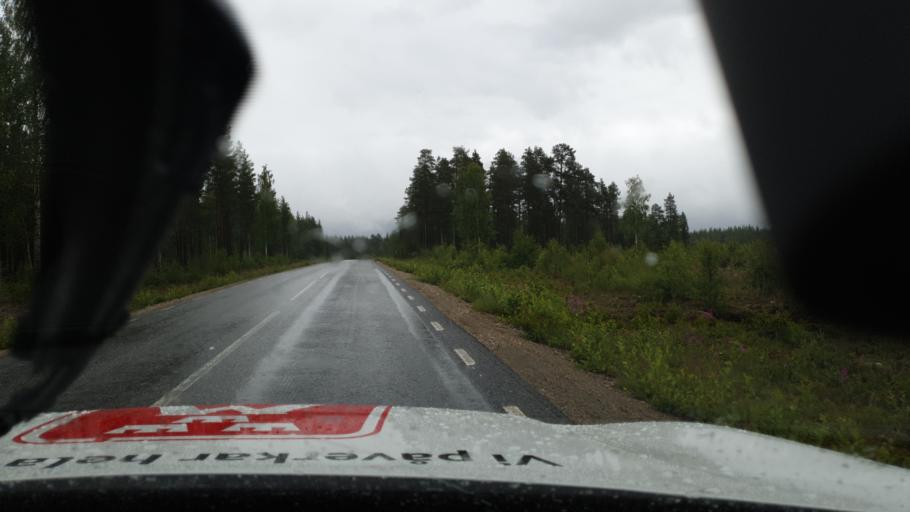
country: SE
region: Vaesterbotten
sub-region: Vindelns Kommun
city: Vindeln
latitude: 64.5429
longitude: 19.9095
